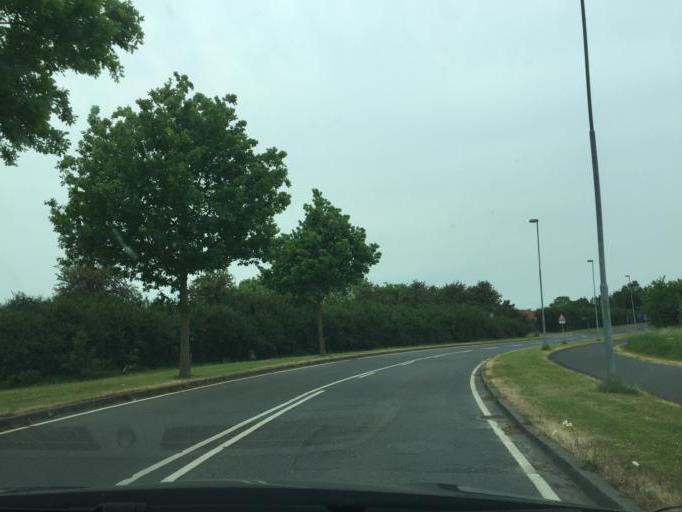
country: DK
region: South Denmark
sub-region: Odense Kommune
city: Neder Holluf
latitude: 55.3598
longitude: 10.4758
